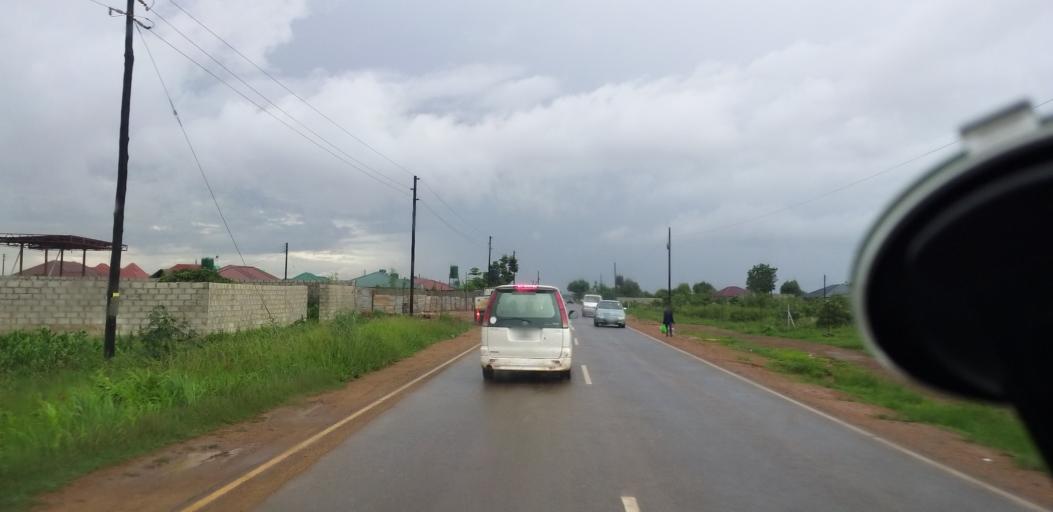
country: ZM
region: Lusaka
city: Lusaka
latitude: -15.4841
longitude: 28.3152
